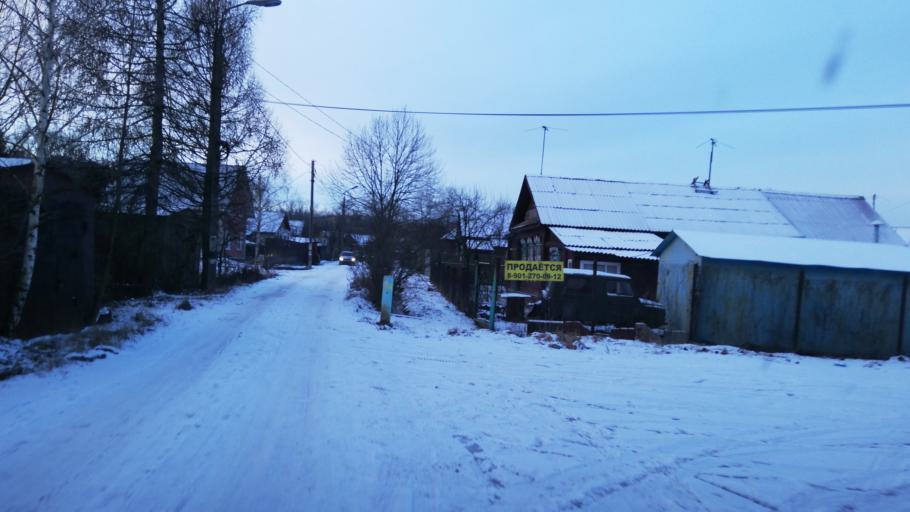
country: RU
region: Jaroslavl
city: Yaroslavl
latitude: 57.5952
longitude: 39.8401
